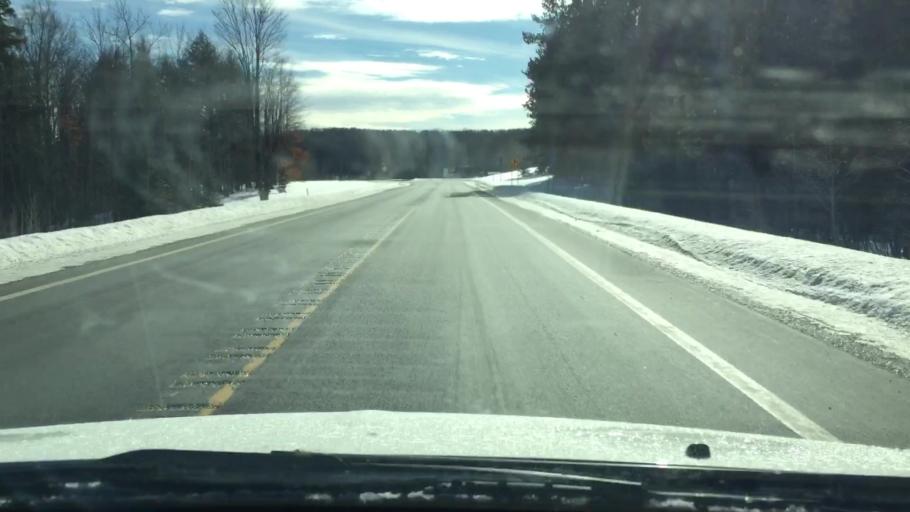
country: US
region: Michigan
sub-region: Antrim County
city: Mancelona
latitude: 44.9955
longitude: -85.0617
